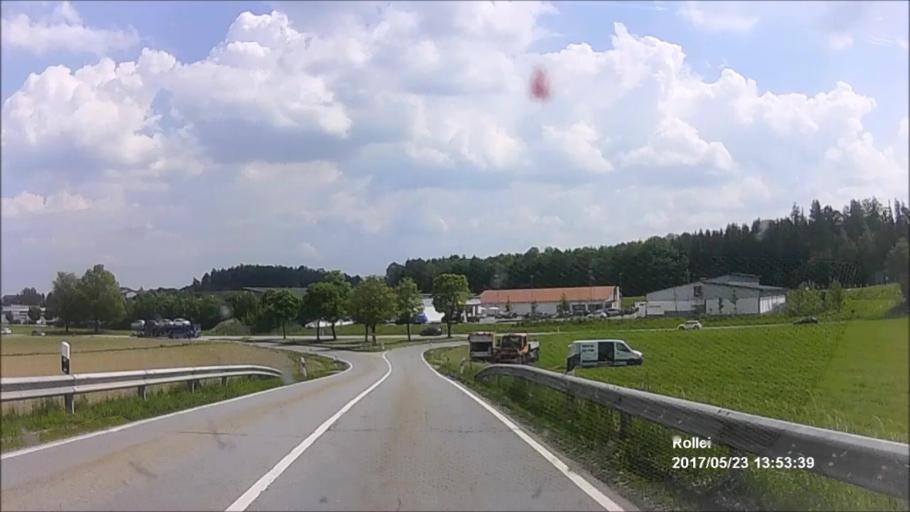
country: DE
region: Bavaria
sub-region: Upper Bavaria
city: Haag in Oberbayern
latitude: 48.1666
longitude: 12.1645
